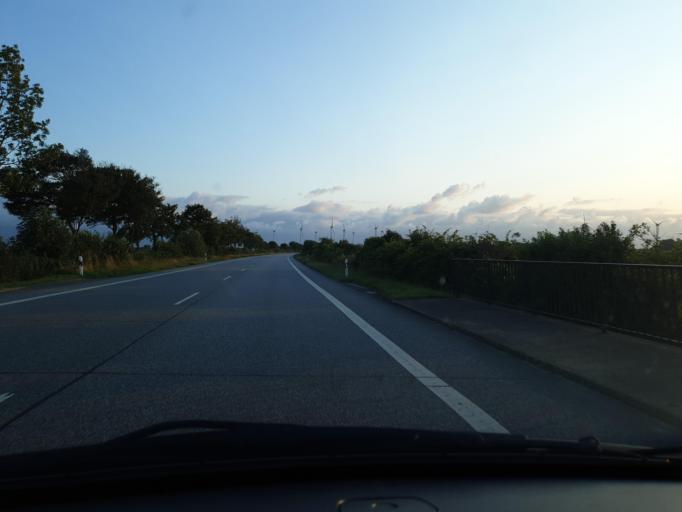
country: DE
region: Schleswig-Holstein
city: Brunsbuttel
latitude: 53.9118
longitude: 9.1132
